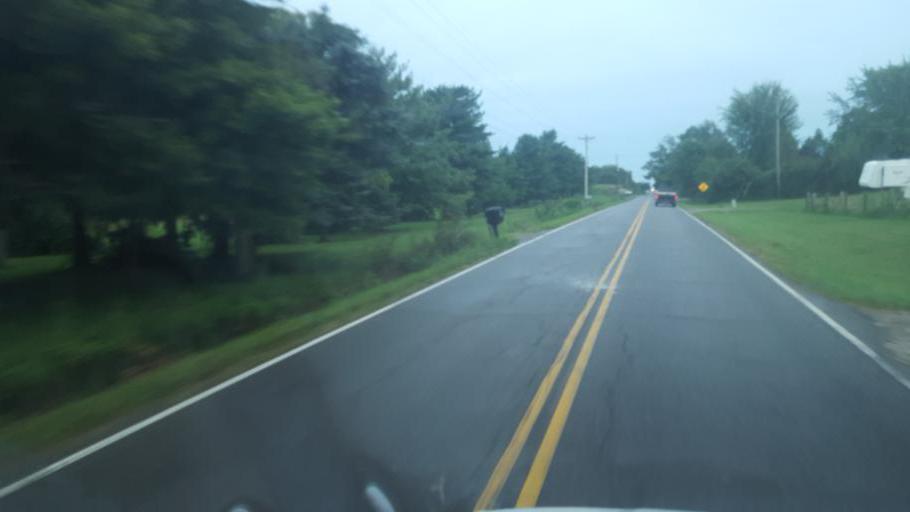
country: US
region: Ohio
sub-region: Licking County
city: Johnstown
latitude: 40.1581
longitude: -82.6441
